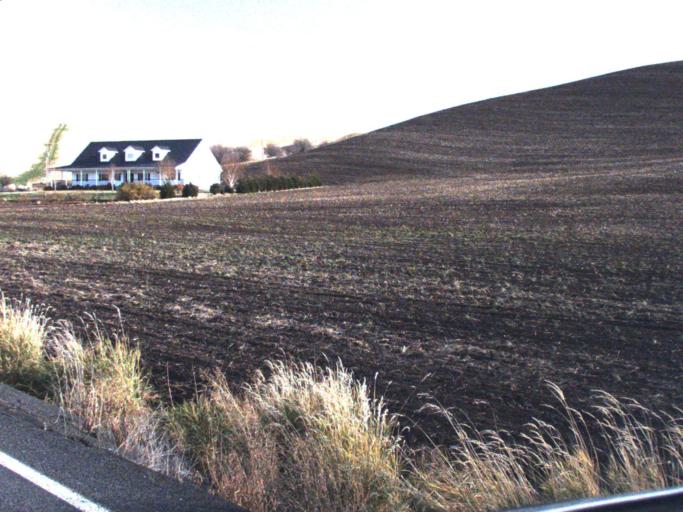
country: US
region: Washington
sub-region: Whitman County
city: Colfax
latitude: 46.7487
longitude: -117.4596
